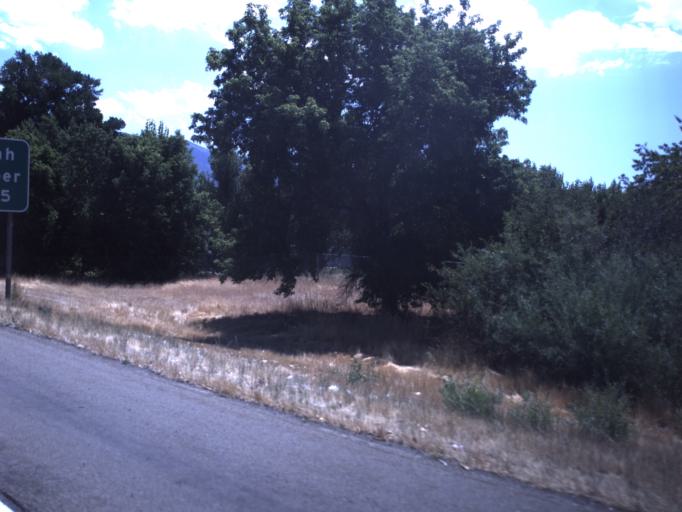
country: US
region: Utah
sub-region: Weber County
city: Washington Terrace
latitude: 41.1531
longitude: -111.9807
